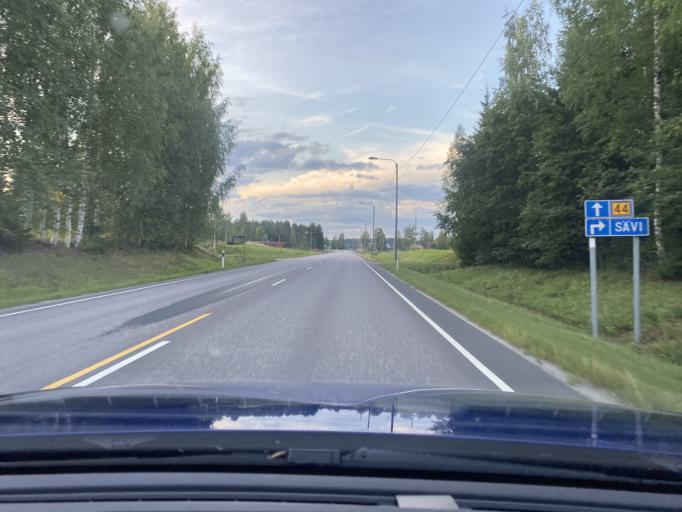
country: FI
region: Satakunta
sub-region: Pohjois-Satakunta
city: Kankaanpaeae
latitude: 61.7399
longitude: 22.5251
